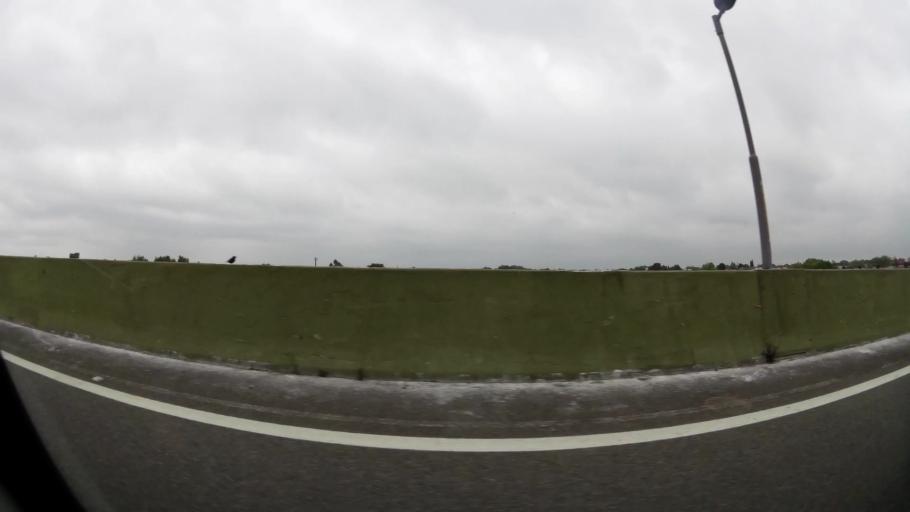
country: AR
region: Buenos Aires
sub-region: Partido de La Plata
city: La Plata
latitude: -34.8812
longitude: -57.9611
